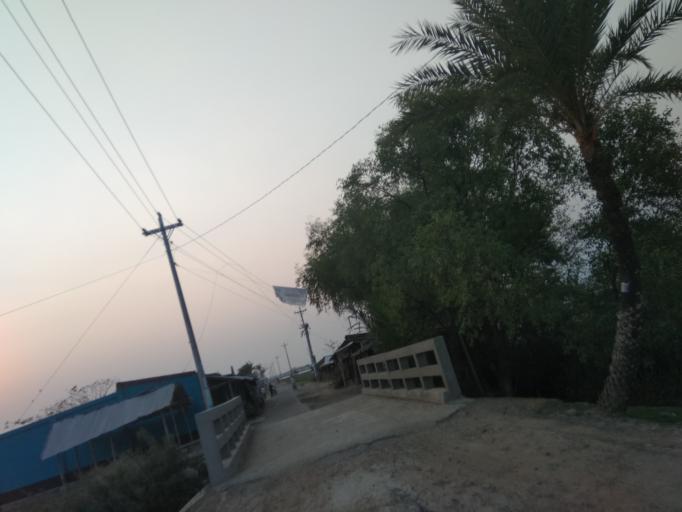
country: IN
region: West Bengal
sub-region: North 24 Parganas
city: Taki
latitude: 22.4566
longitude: 89.0733
